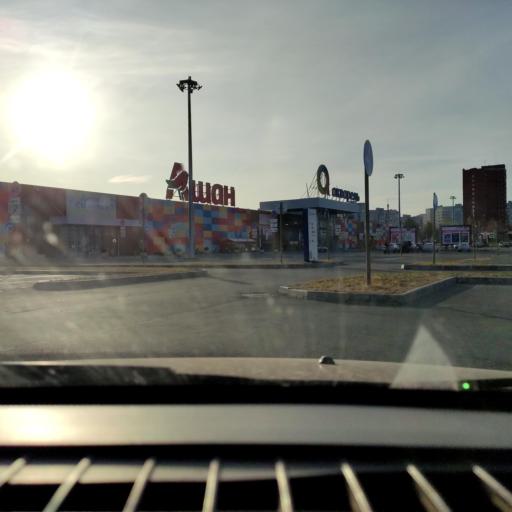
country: RU
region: Samara
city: Tol'yatti
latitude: 53.5510
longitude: 49.3437
